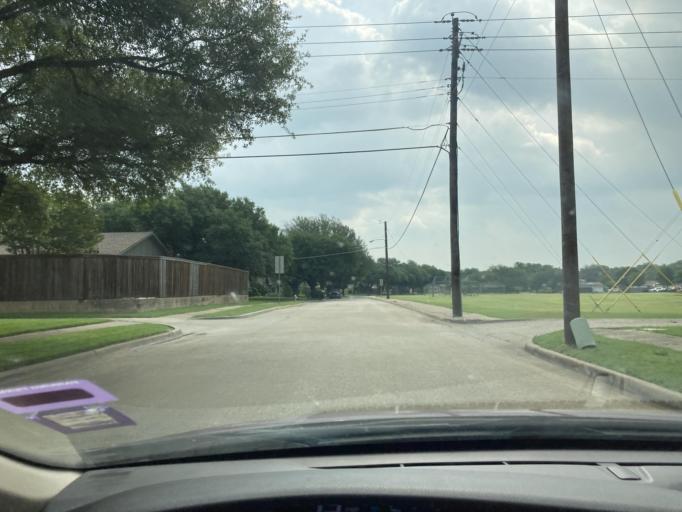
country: US
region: Texas
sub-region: Collin County
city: Plano
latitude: 33.0526
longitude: -96.7240
